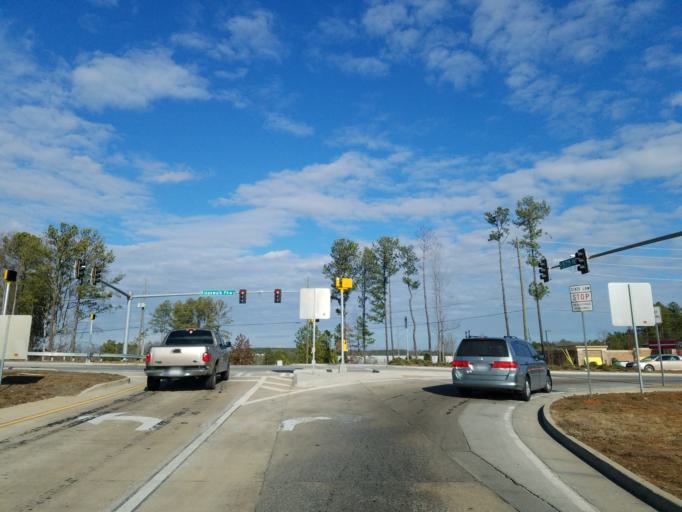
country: US
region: Georgia
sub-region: Cherokee County
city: Woodstock
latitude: 34.1232
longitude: -84.5259
